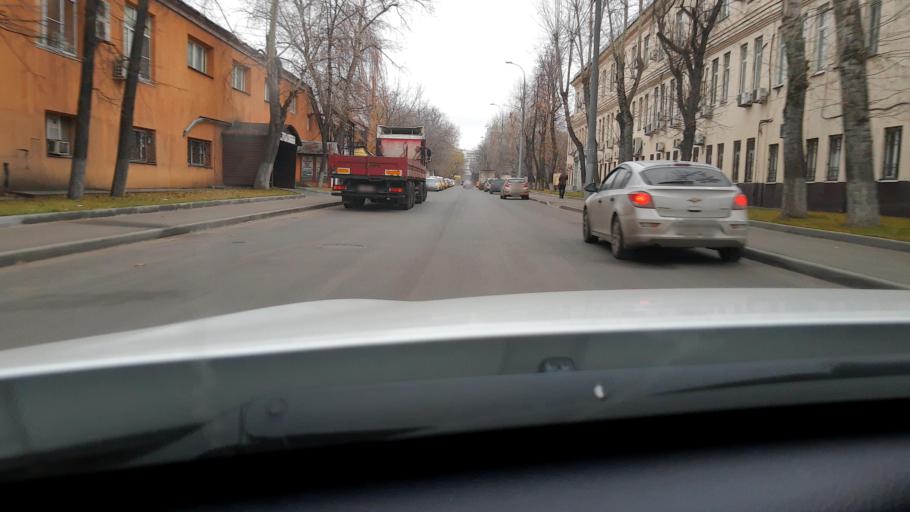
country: RU
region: Moscow
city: Ryazanskiy
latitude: 55.7208
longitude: 37.7548
